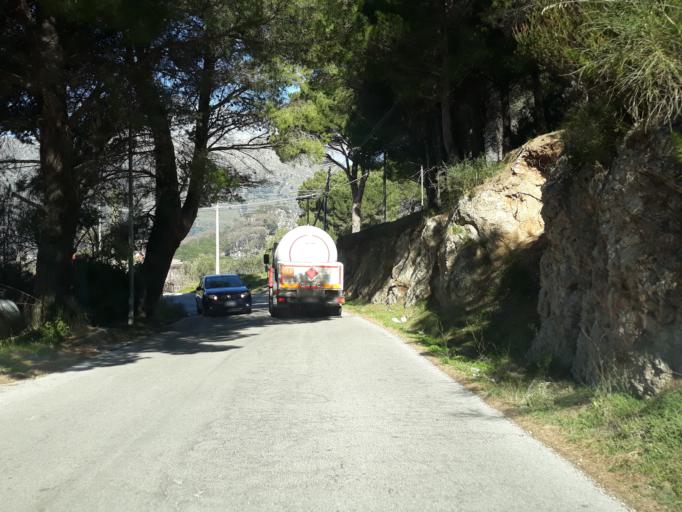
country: IT
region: Sicily
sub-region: Palermo
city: Piano dei Geli
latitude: 38.0833
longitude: 13.2703
